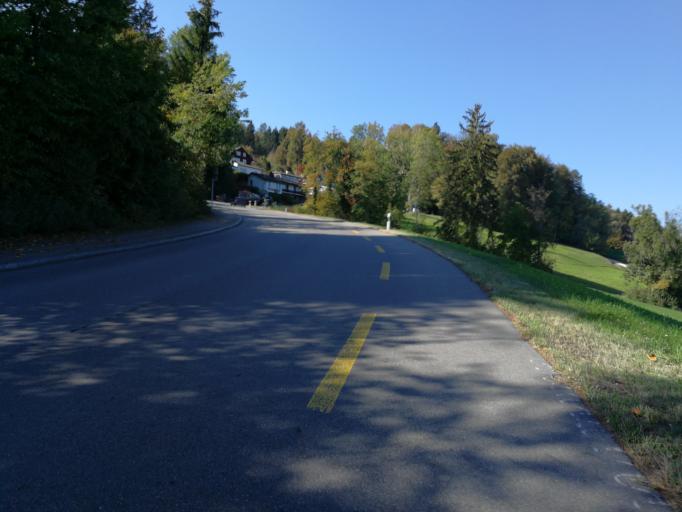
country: CH
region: Zurich
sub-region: Bezirk Uster
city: Aesch
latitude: 47.3430
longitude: 8.6625
